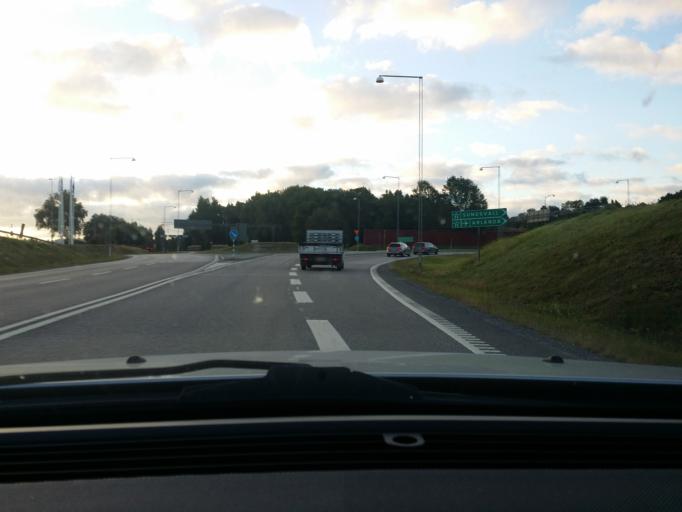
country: SE
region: Stockholm
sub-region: Upplands Vasby Kommun
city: Upplands Vaesby
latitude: 59.4699
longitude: 17.9136
